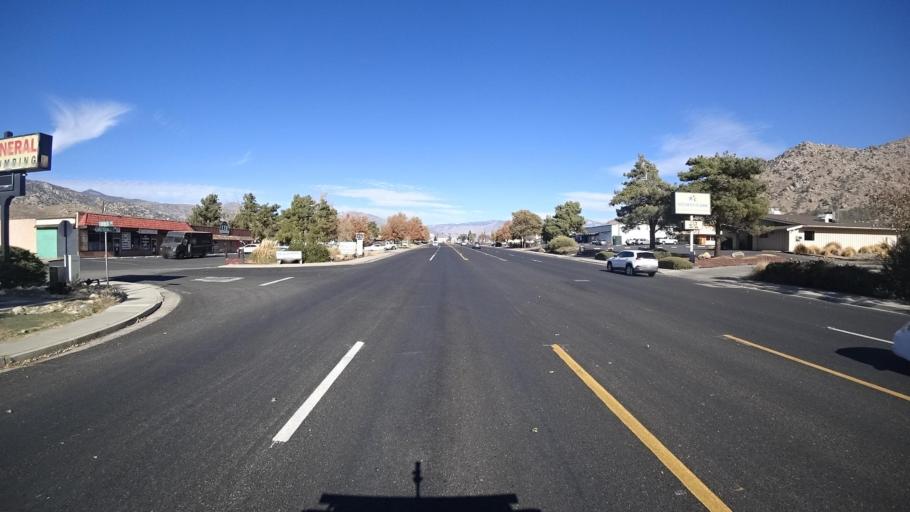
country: US
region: California
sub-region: Kern County
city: Lake Isabella
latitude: 35.6249
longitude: -118.4723
